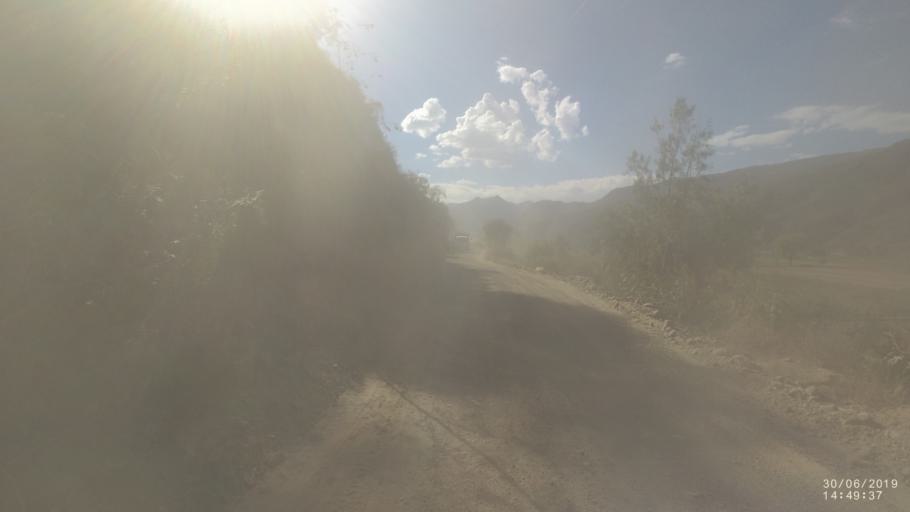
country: BO
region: Cochabamba
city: Irpa Irpa
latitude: -17.7821
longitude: -66.3421
